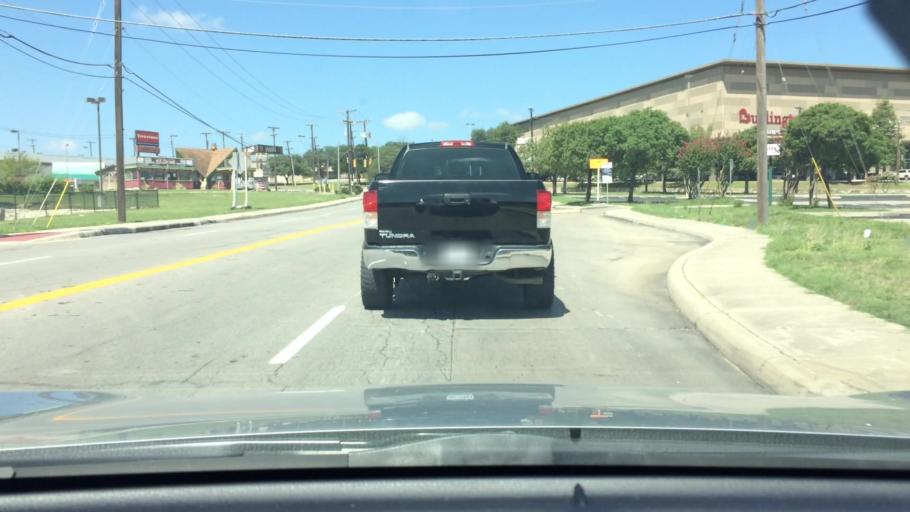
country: US
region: Texas
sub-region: Bexar County
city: Balcones Heights
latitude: 29.4927
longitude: -98.5479
